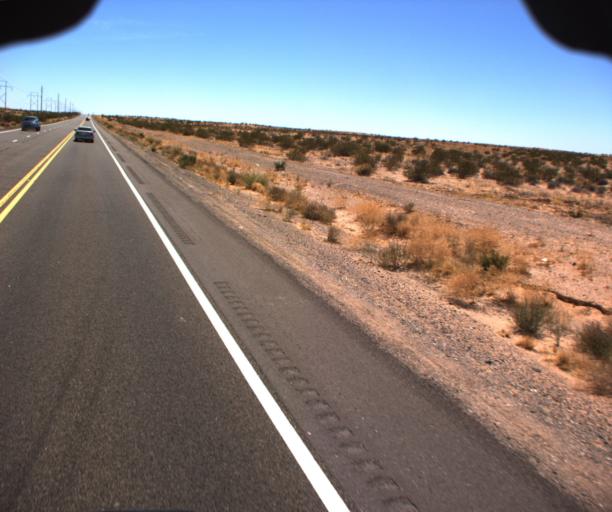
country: US
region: Arizona
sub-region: La Paz County
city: Parker
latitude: 33.9664
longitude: -114.2169
